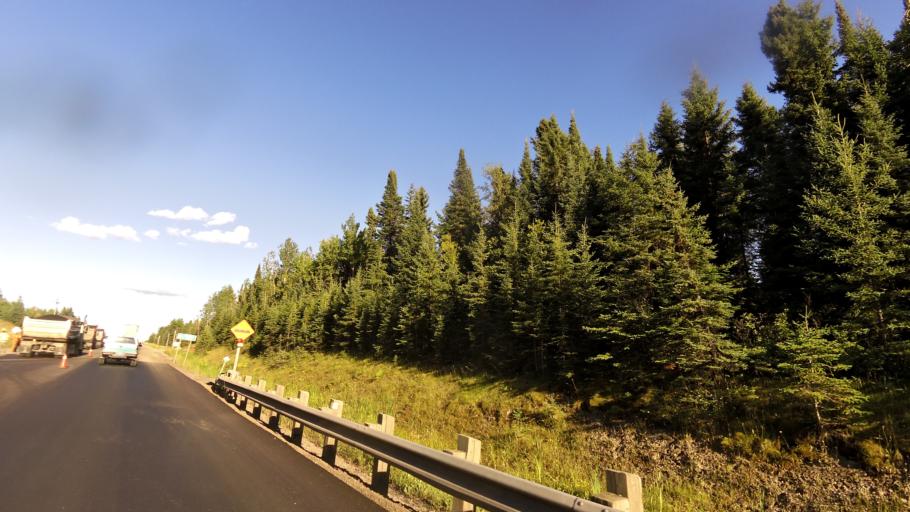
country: CA
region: Ontario
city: Dryden
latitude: 49.8151
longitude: -92.8722
